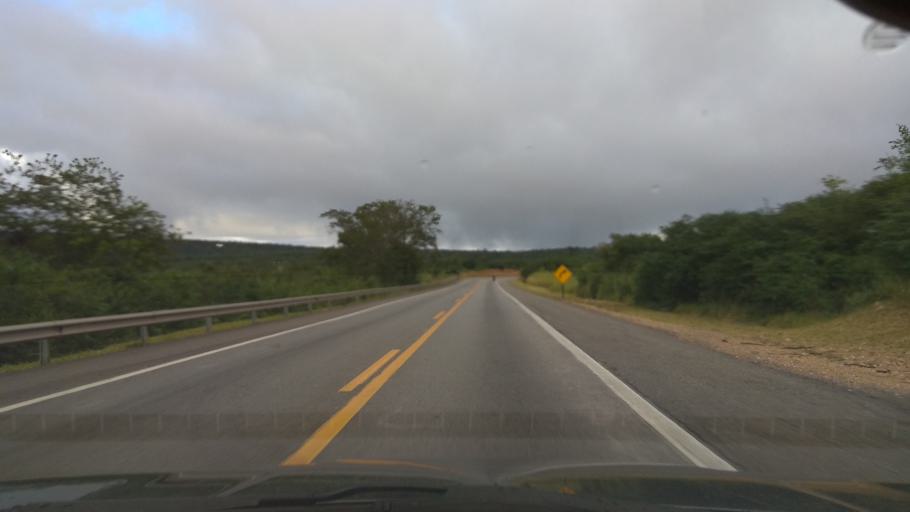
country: BR
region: Bahia
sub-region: Santa Ines
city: Santa Ines
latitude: -13.3125
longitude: -40.0199
